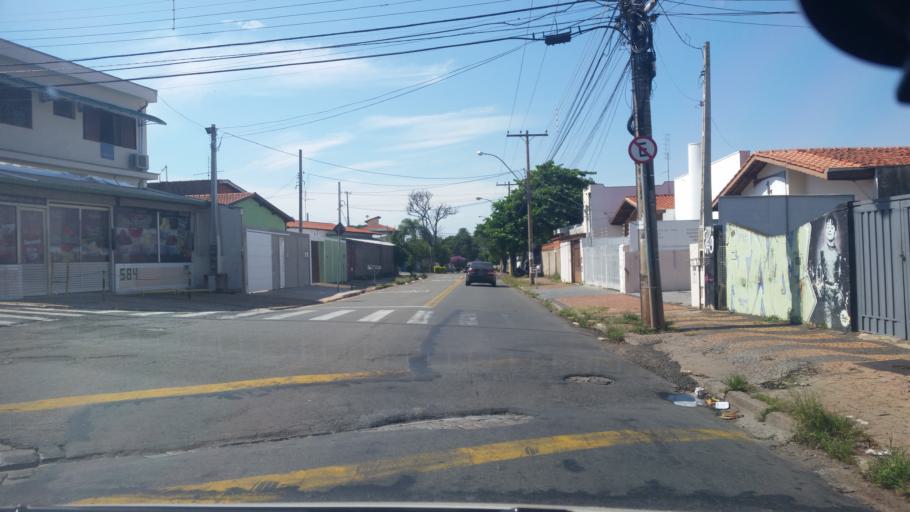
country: BR
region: Sao Paulo
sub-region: Campinas
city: Campinas
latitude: -22.8654
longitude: -47.0660
